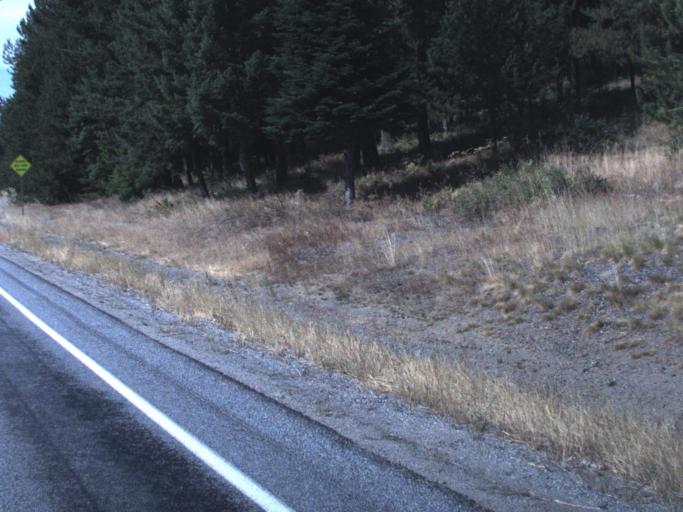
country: US
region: Washington
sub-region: Pend Oreille County
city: Newport
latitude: 48.1500
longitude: -117.3015
